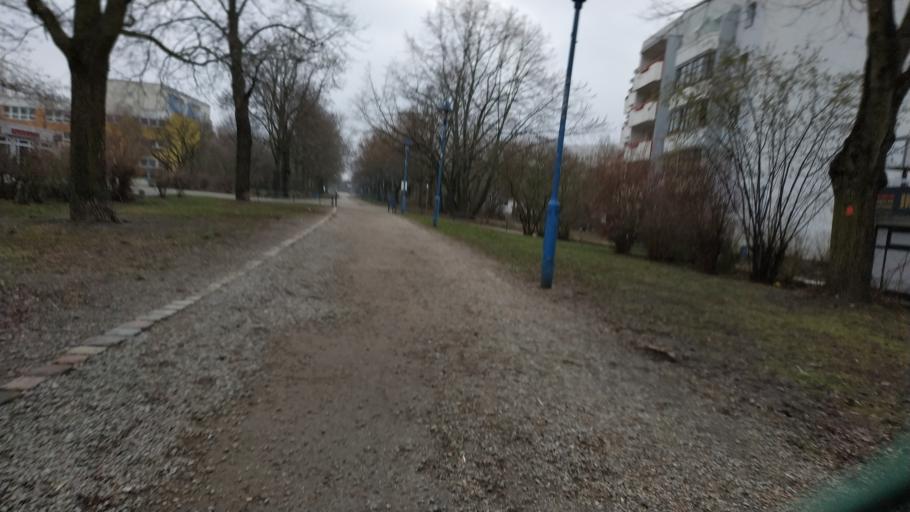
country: DE
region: Berlin
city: Hellersdorf
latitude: 52.5312
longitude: 13.6038
